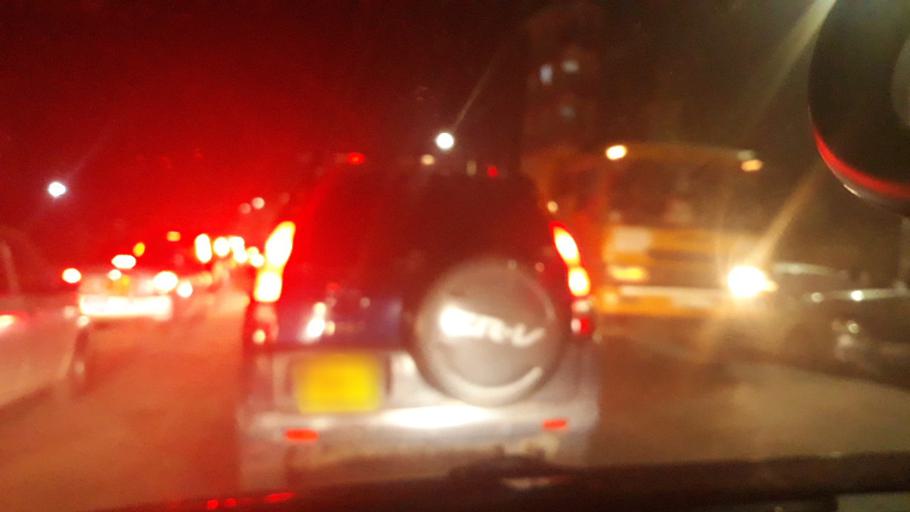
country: KE
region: Nairobi Area
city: Pumwani
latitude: -1.2781
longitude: 36.8843
